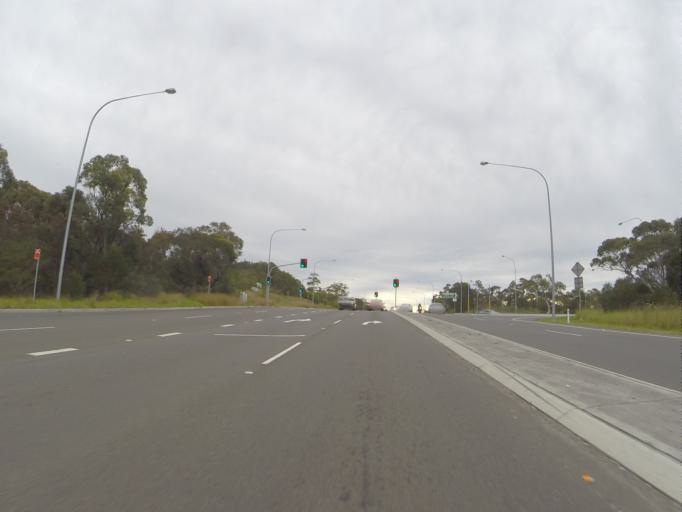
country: AU
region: New South Wales
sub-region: Sutherland Shire
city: Engadine
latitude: -34.0525
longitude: 150.9723
